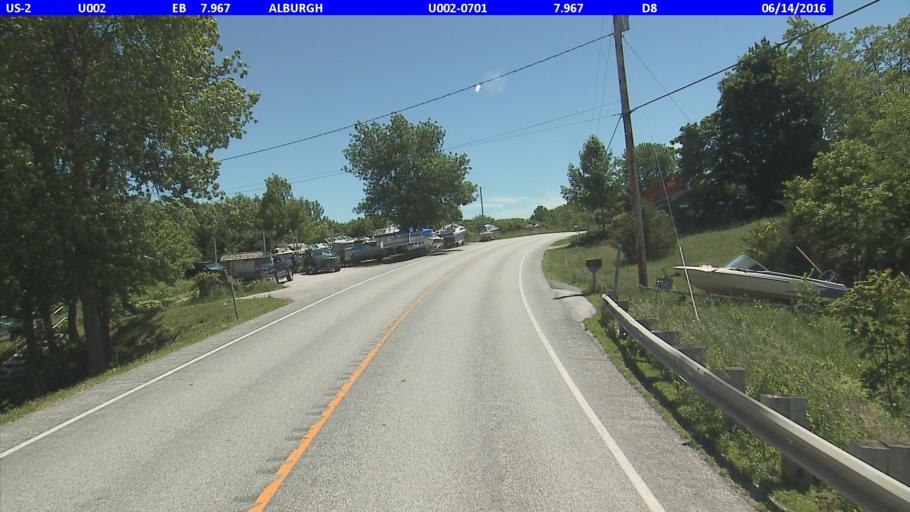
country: US
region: New York
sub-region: Clinton County
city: Rouses Point
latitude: 44.9361
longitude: -73.2733
